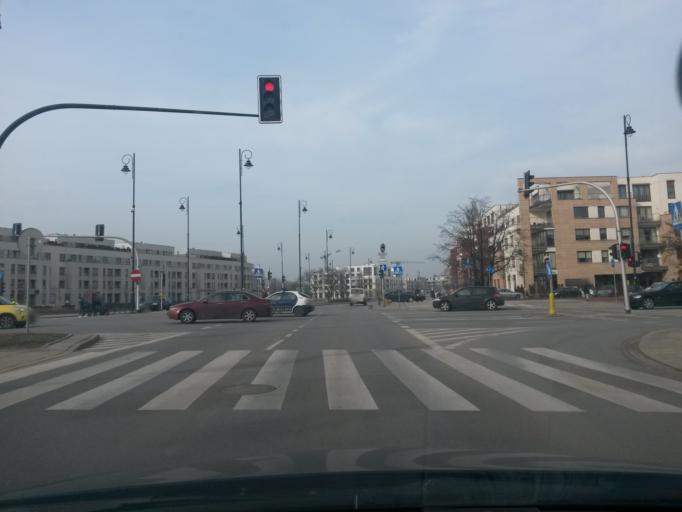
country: PL
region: Masovian Voivodeship
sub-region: Warszawa
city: Wilanow
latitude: 52.1601
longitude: 21.0727
